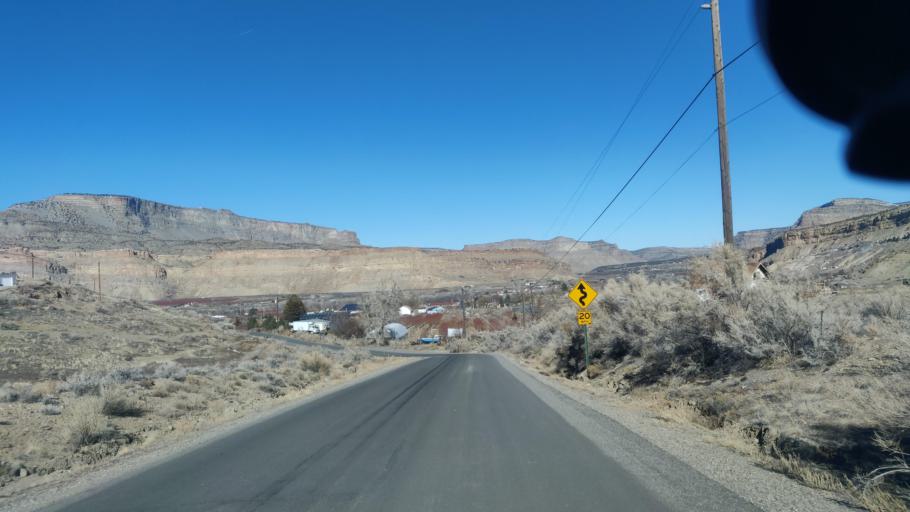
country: US
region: Colorado
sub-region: Mesa County
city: Palisade
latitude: 39.0978
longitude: -108.3296
